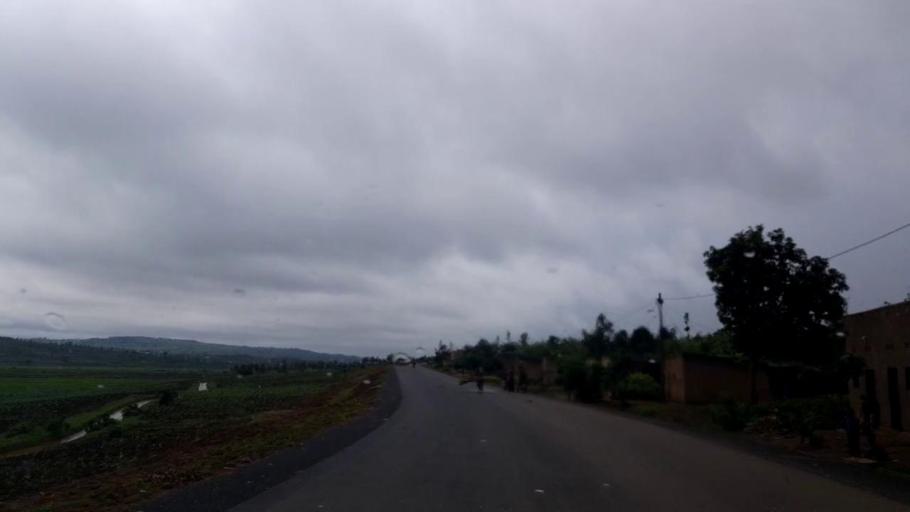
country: RW
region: Northern Province
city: Byumba
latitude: -1.4264
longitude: 30.2766
